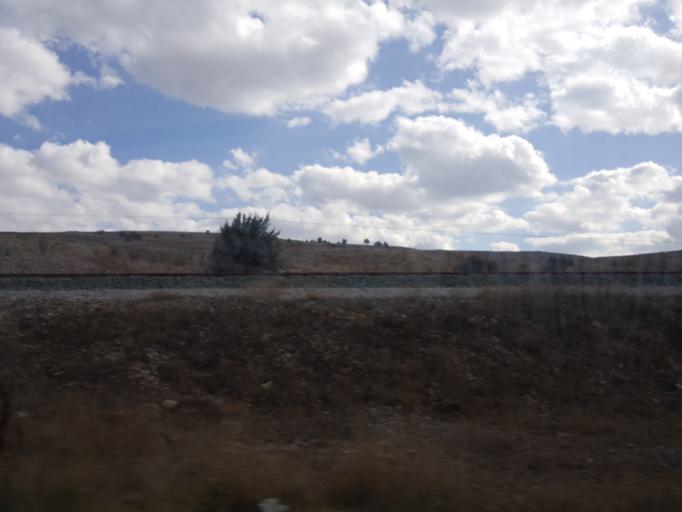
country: TR
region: Tokat
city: Yesilyurt
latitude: 40.0159
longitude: 36.2450
